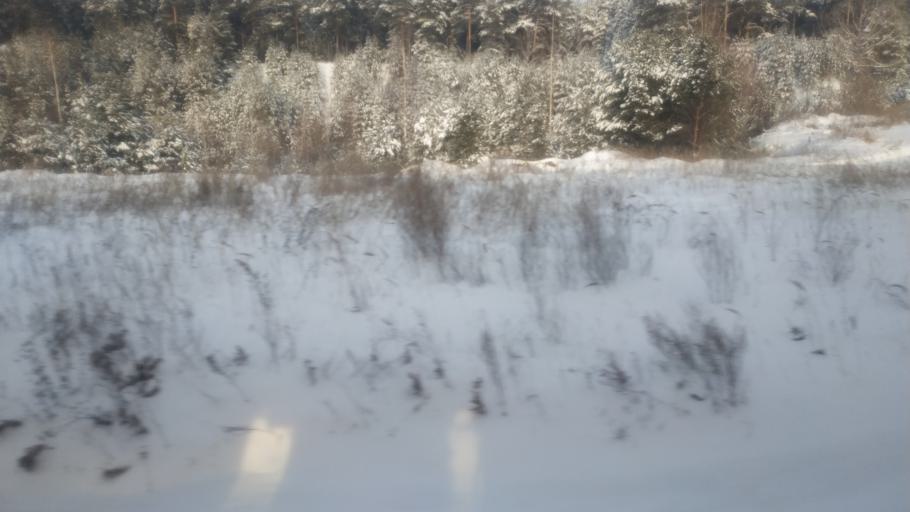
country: RU
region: Kirov
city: Krasnaya Polyana
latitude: 56.2475
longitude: 51.1612
